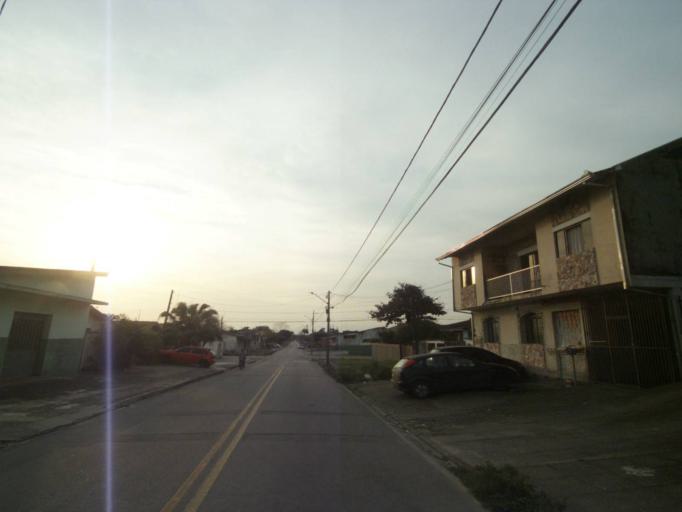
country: BR
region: Parana
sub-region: Paranagua
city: Paranagua
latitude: -25.5206
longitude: -48.5389
